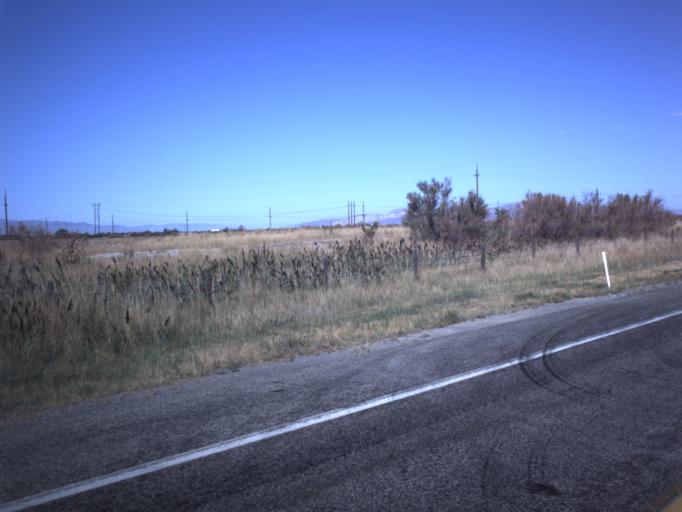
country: US
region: Utah
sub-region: Salt Lake County
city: Magna
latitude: 40.7377
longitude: -112.1741
